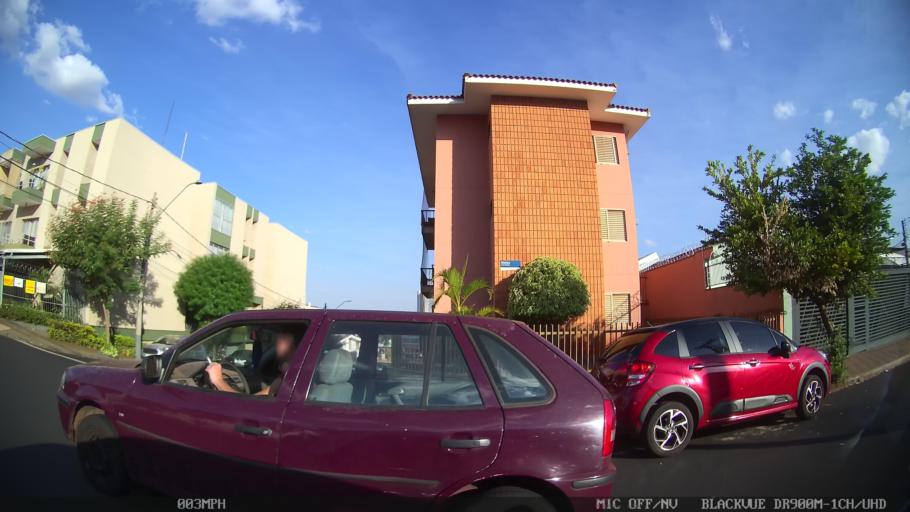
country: BR
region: Sao Paulo
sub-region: Ribeirao Preto
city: Ribeirao Preto
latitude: -21.1866
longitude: -47.7919
